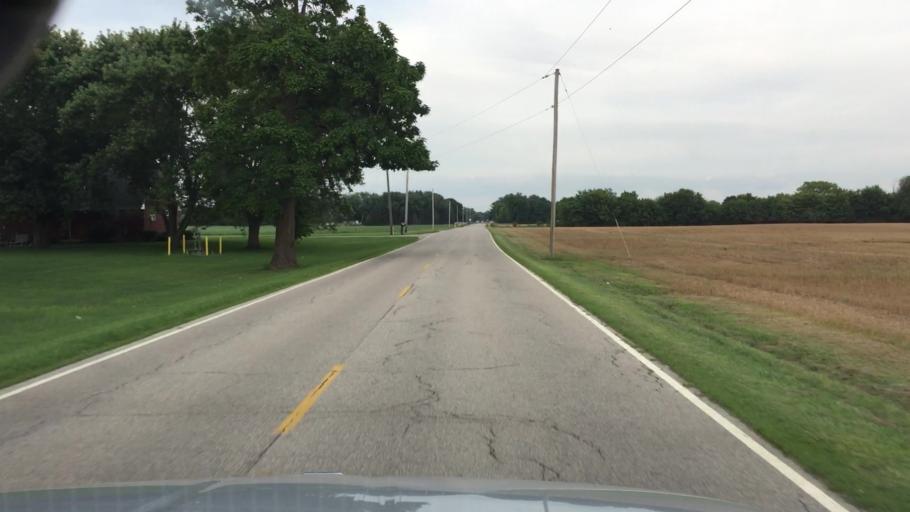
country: US
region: Ohio
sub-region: Madison County
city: Plain City
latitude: 40.0741
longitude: -83.2370
